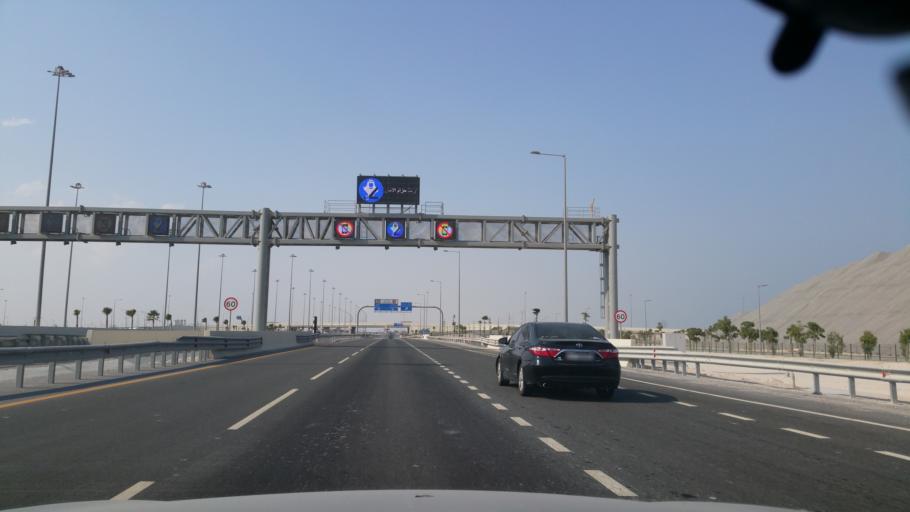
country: QA
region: Baladiyat Umm Salal
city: Umm Salal Muhammad
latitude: 25.4507
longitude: 51.4800
